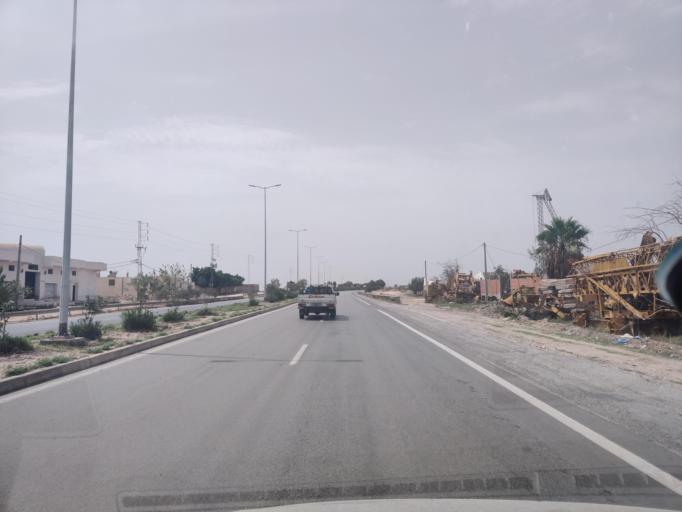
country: TN
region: Susah
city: Akouda
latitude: 35.8360
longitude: 10.5532
